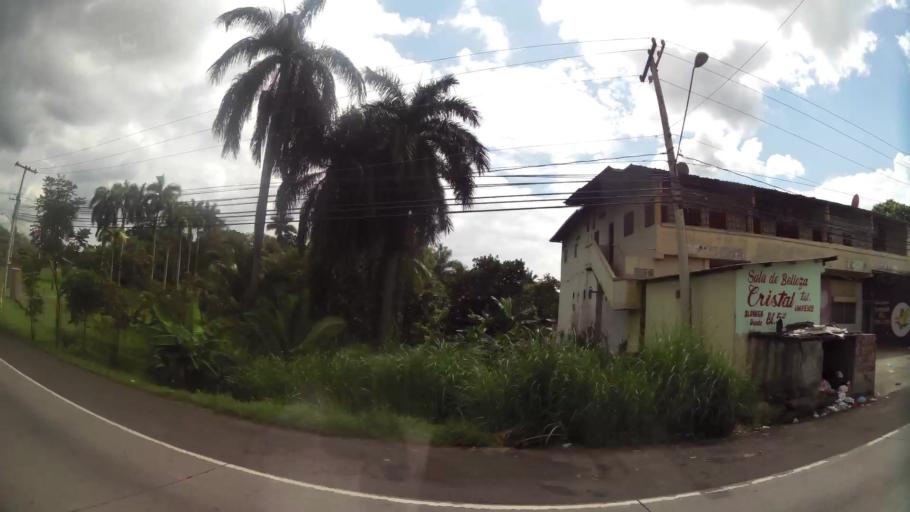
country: PA
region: Panama
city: Nuevo Arraijan
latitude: 8.9269
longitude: -79.7335
